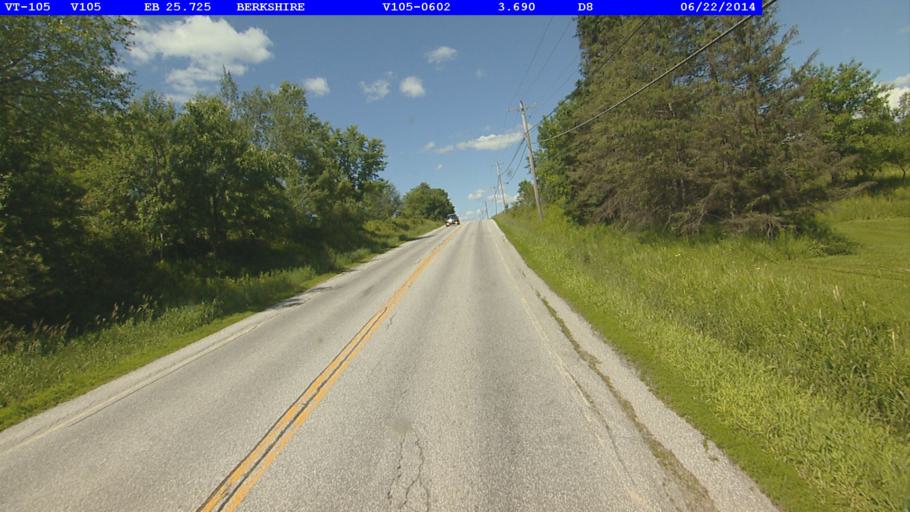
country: US
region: Vermont
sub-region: Franklin County
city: Richford
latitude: 44.9715
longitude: -72.6890
